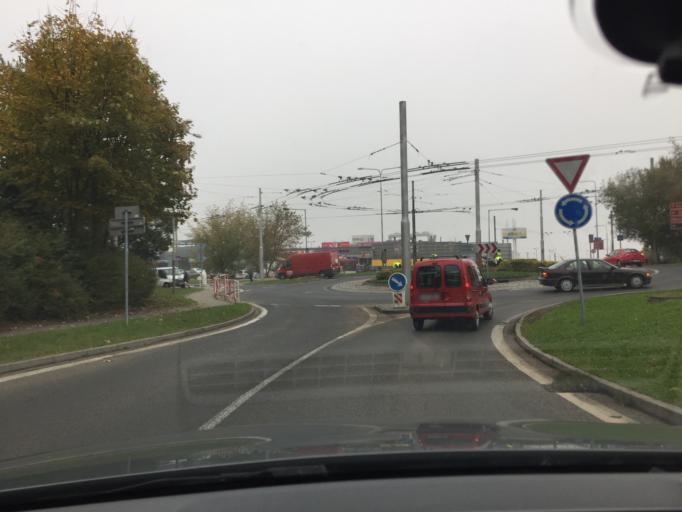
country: CZ
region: Ustecky
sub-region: Okres Usti nad Labem
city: Usti nad Labem
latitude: 50.6792
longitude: 14.0369
